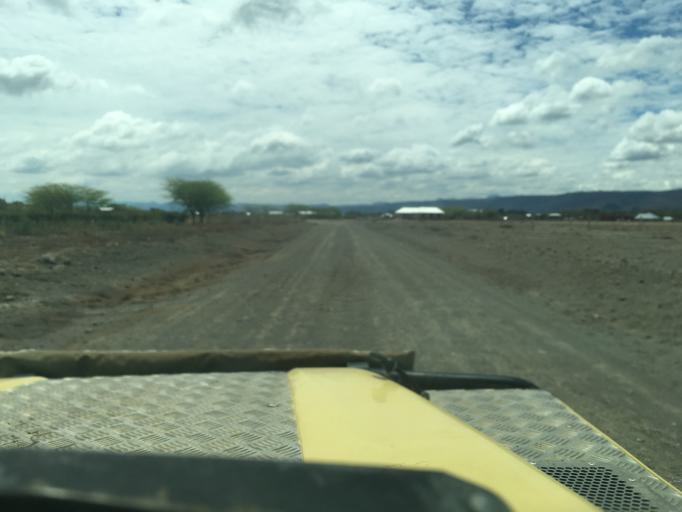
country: TZ
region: Arusha
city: Mto wa Mbu
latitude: -3.3621
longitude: 35.8950
